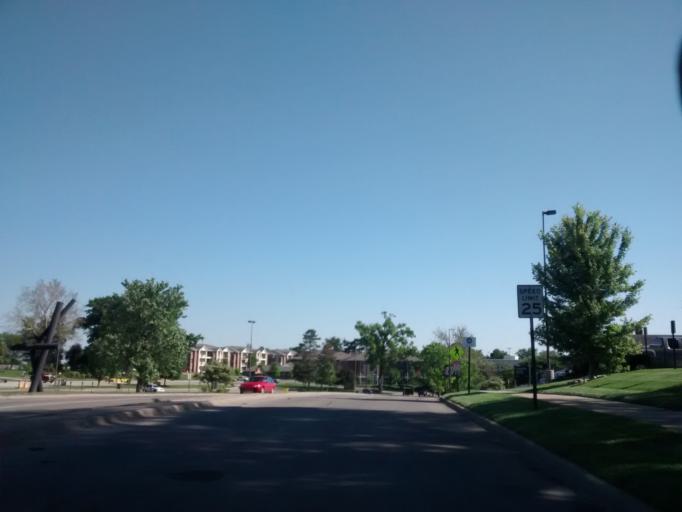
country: US
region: Nebraska
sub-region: Douglas County
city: Ralston
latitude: 41.2595
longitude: -96.0150
